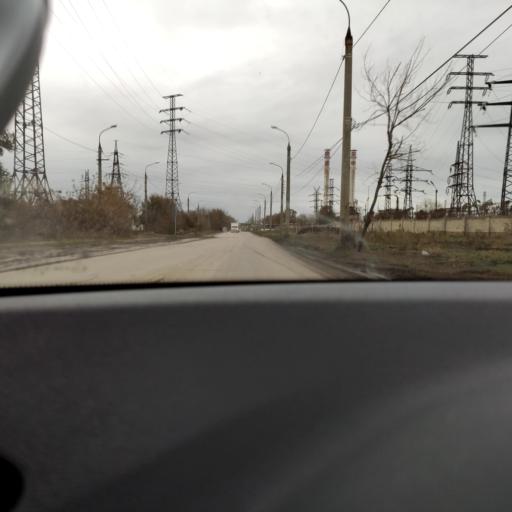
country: RU
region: Samara
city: Smyshlyayevka
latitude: 53.2005
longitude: 50.2894
